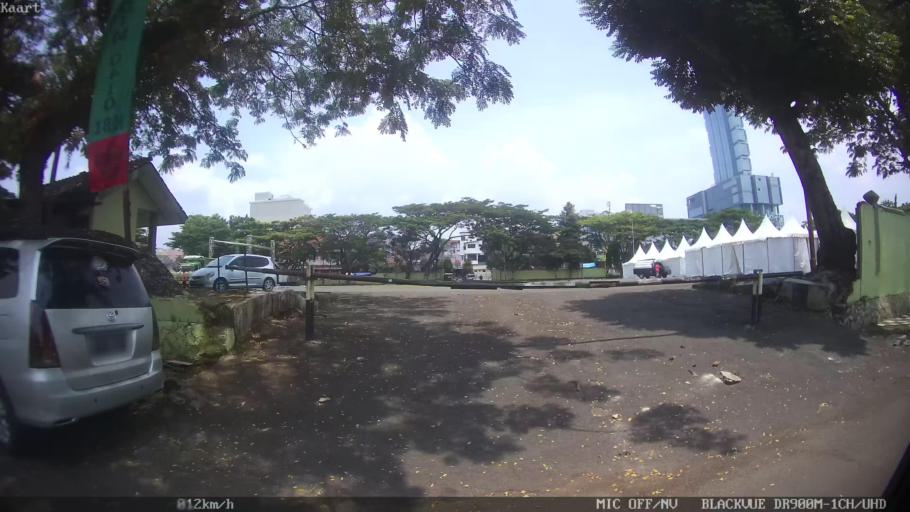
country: ID
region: Lampung
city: Bandarlampung
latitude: -5.4193
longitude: 105.2603
